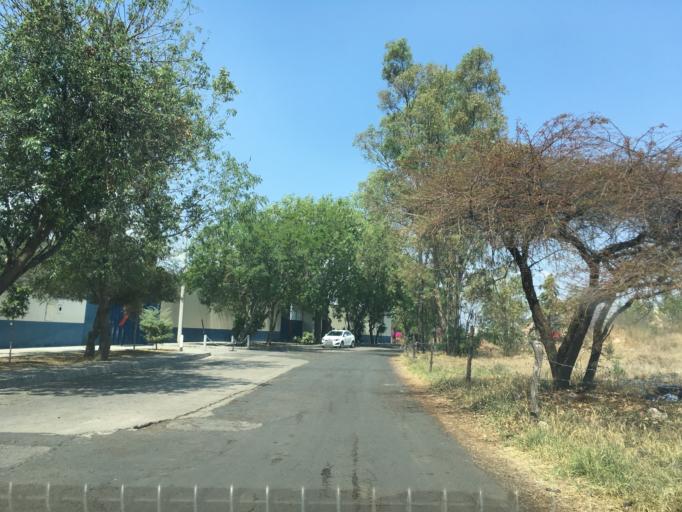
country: MX
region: Michoacan
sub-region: Morelia
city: Morelos
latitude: 19.6692
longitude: -101.2091
